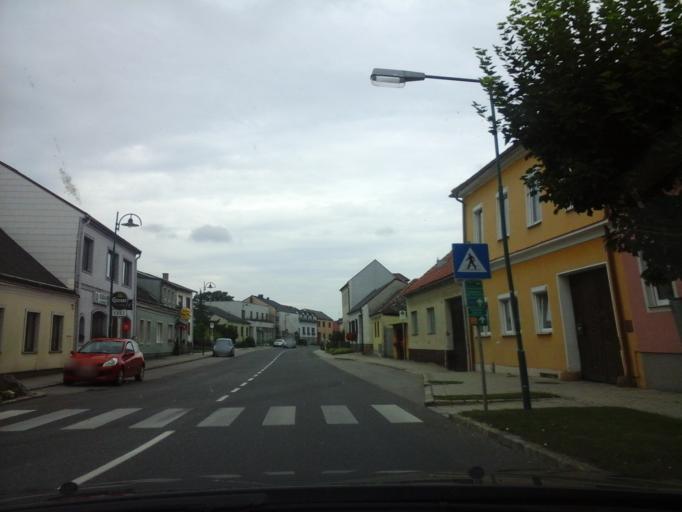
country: AT
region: Lower Austria
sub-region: Politischer Bezirk Bruck an der Leitha
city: Prellenkirchen
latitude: 48.0750
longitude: 16.9516
